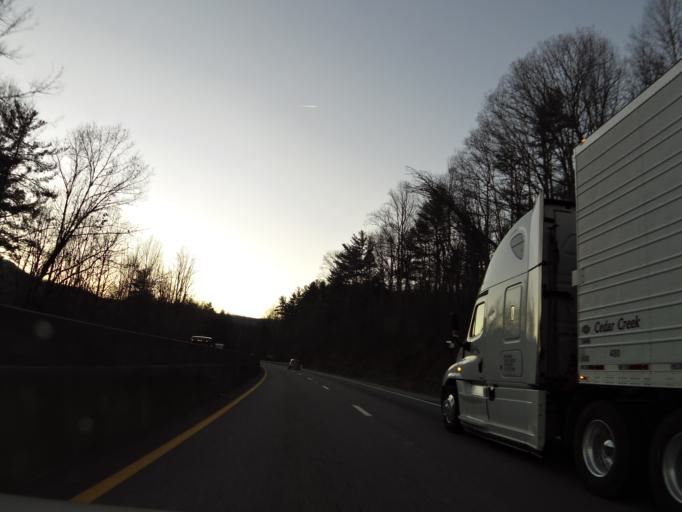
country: US
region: North Carolina
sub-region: Haywood County
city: Cove Creek
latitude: 35.6719
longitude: -83.0043
